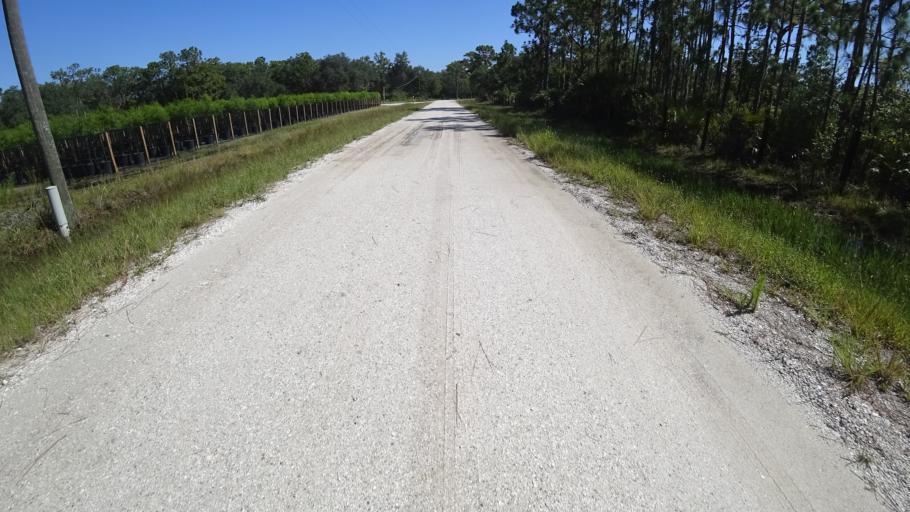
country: US
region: Florida
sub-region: Sarasota County
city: The Meadows
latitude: 27.4116
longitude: -82.2956
